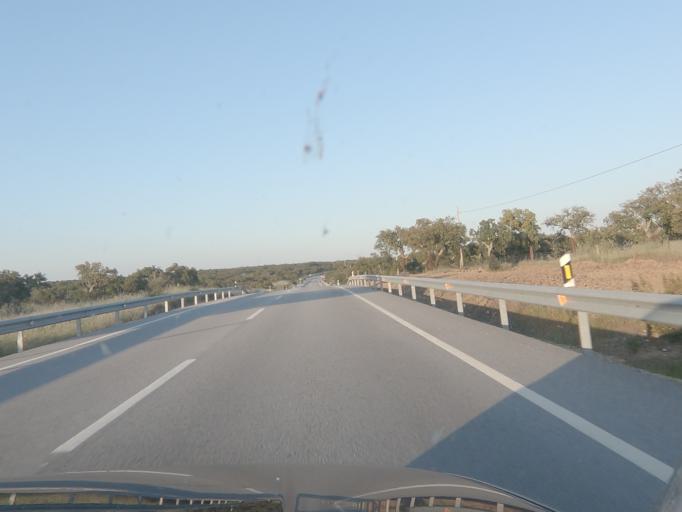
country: ES
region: Extremadura
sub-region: Provincia de Caceres
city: Carbajo
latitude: 39.5055
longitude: -7.1536
